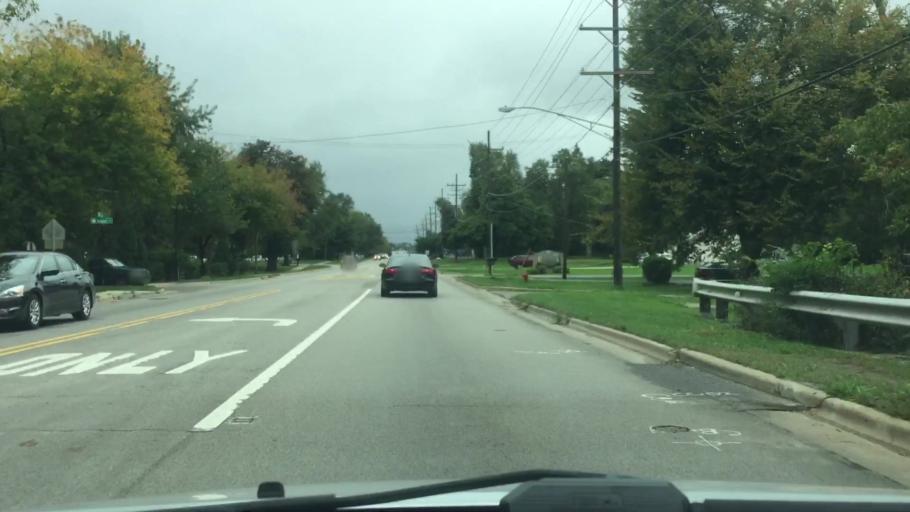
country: US
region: Illinois
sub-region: McHenry County
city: McHenry
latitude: 42.3355
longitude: -88.2746
